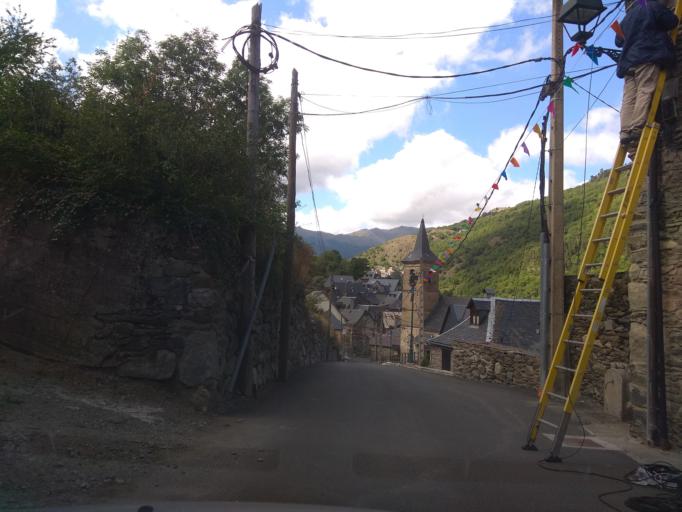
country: ES
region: Catalonia
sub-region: Provincia de Lleida
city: Les
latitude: 42.7371
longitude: 0.7199
